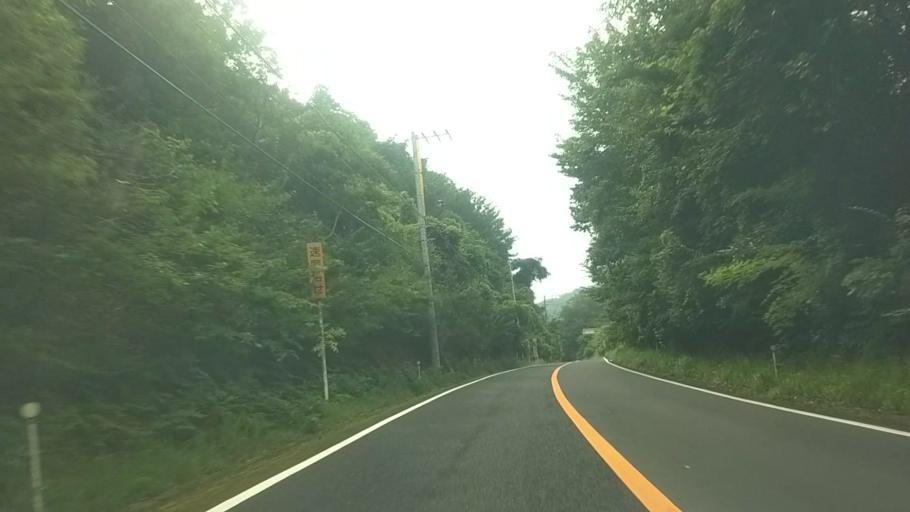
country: JP
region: Chiba
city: Kawaguchi
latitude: 35.2047
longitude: 140.0672
